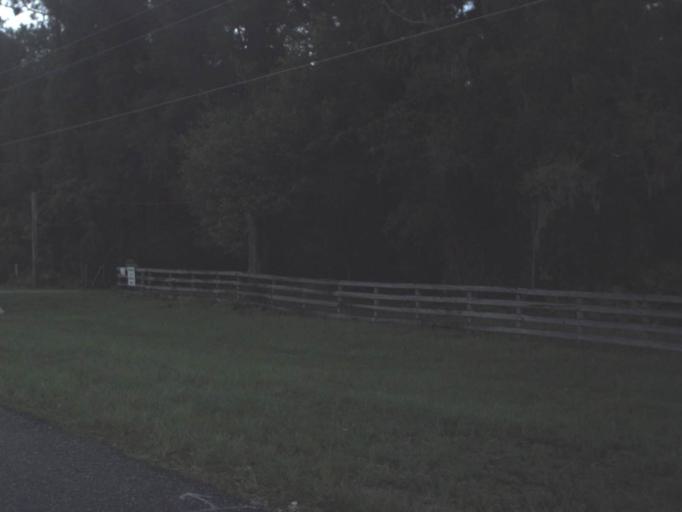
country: US
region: Florida
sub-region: Levy County
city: Inglis
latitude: 29.1131
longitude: -82.6366
